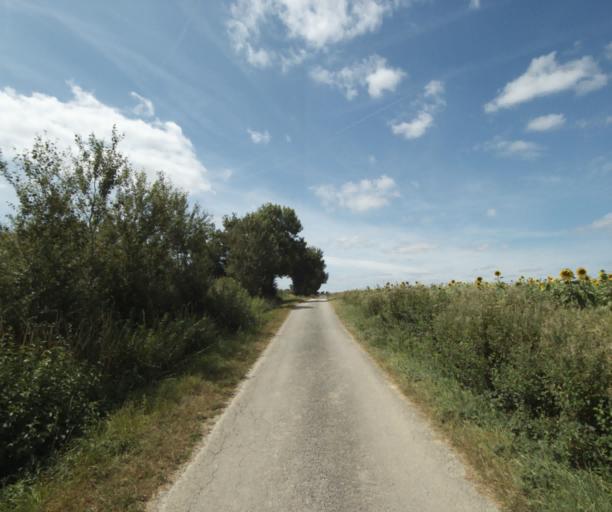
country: FR
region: Midi-Pyrenees
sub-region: Departement du Tarn
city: Soreze
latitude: 43.4840
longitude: 2.0677
